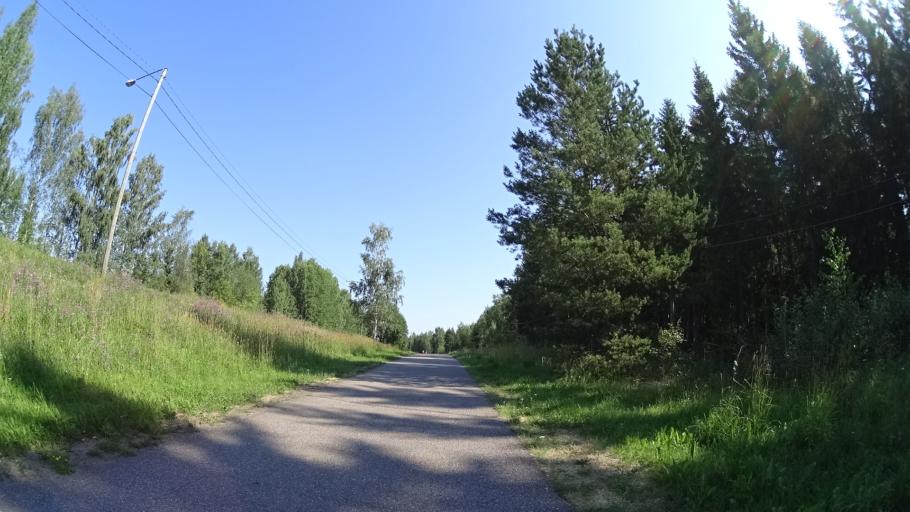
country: FI
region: Uusimaa
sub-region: Helsinki
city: Kerava
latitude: 60.3308
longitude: 25.1240
